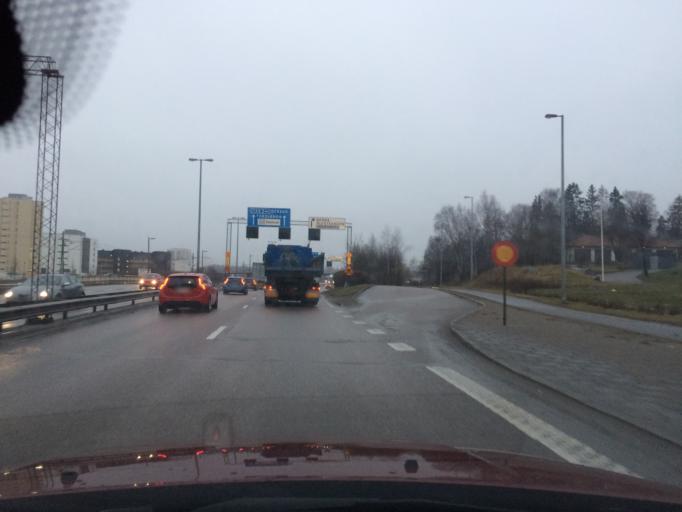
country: SE
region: Vaestra Goetaland
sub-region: Goteborg
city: Majorna
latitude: 57.7116
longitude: 11.9294
